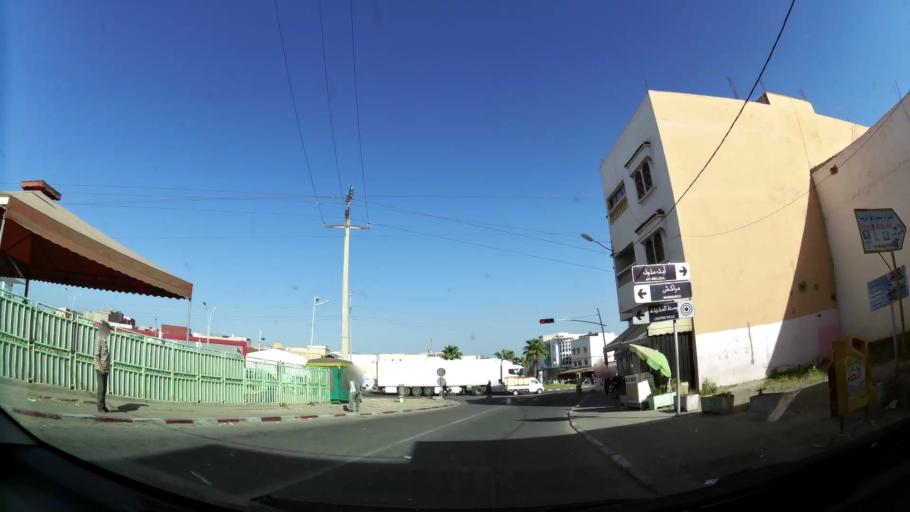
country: MA
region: Souss-Massa-Draa
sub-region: Inezgane-Ait Mellou
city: Inezgane
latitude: 30.3741
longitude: -9.5053
